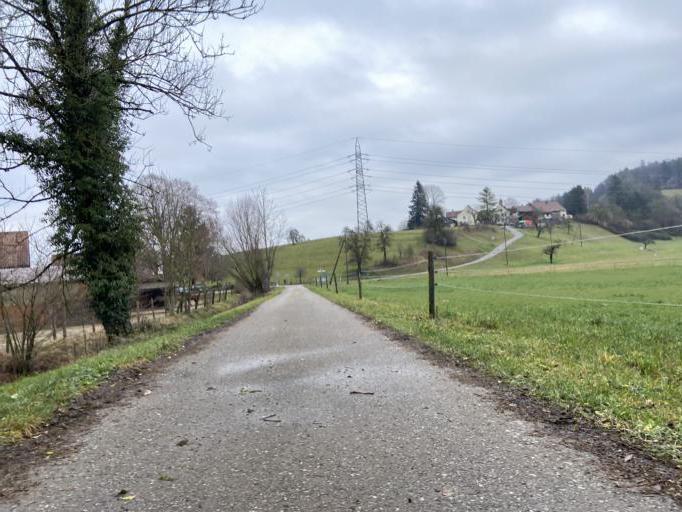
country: CH
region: Zurich
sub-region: Bezirk Winterthur
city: Wuelflingen (Kreis 6) / Niederfeld
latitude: 47.4941
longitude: 8.6739
